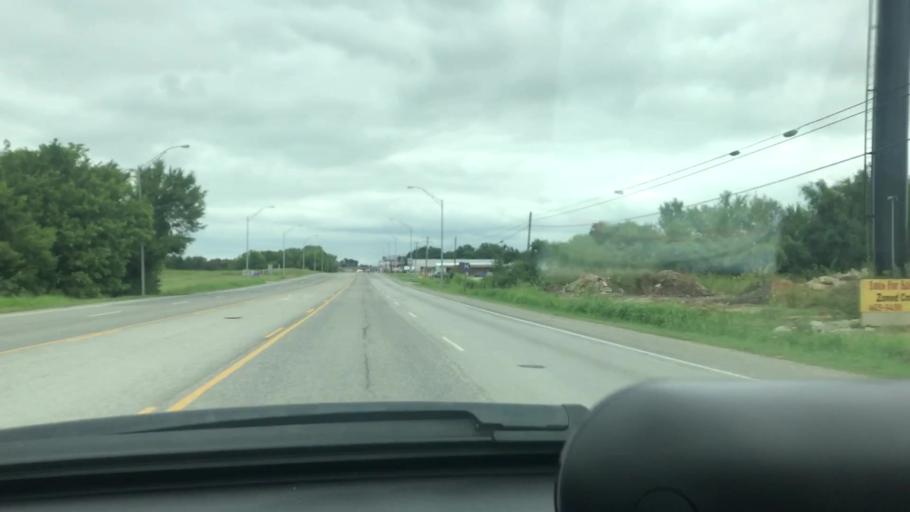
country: US
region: Oklahoma
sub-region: Wagoner County
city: Wagoner
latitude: 35.9495
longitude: -95.3952
